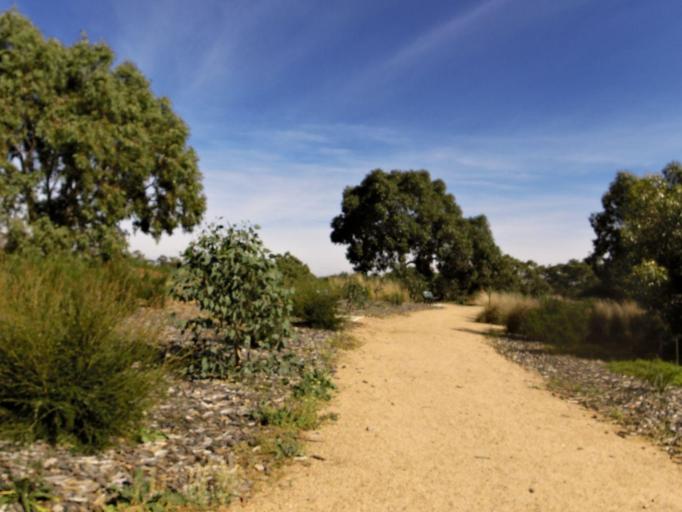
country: AU
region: Victoria
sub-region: Melton
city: Melton
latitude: -37.6924
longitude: 144.5909
